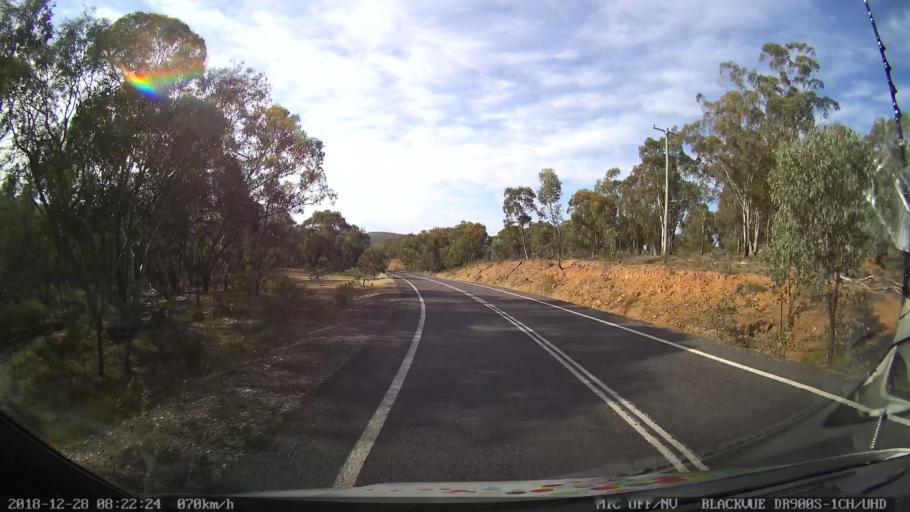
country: AU
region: New South Wales
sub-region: Blayney
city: Blayney
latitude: -33.8929
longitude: 149.3482
